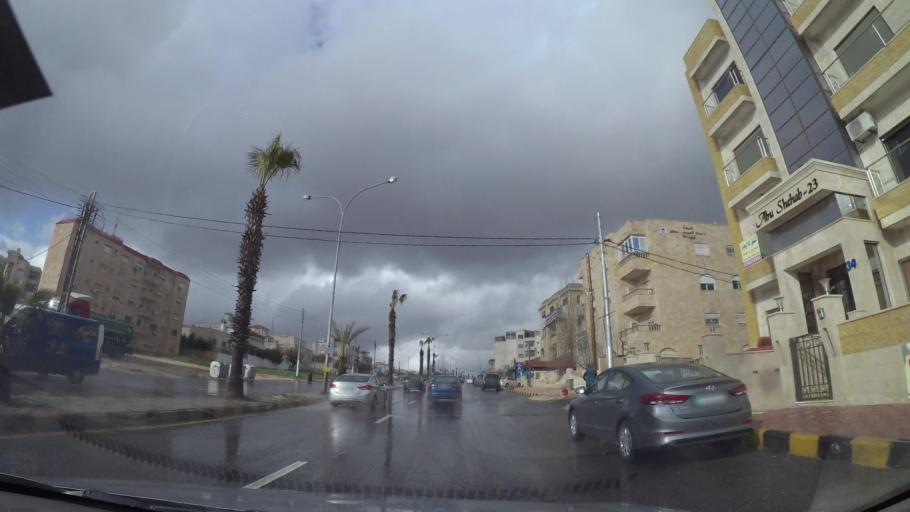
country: JO
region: Amman
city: Al Jubayhah
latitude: 32.0334
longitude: 35.8635
